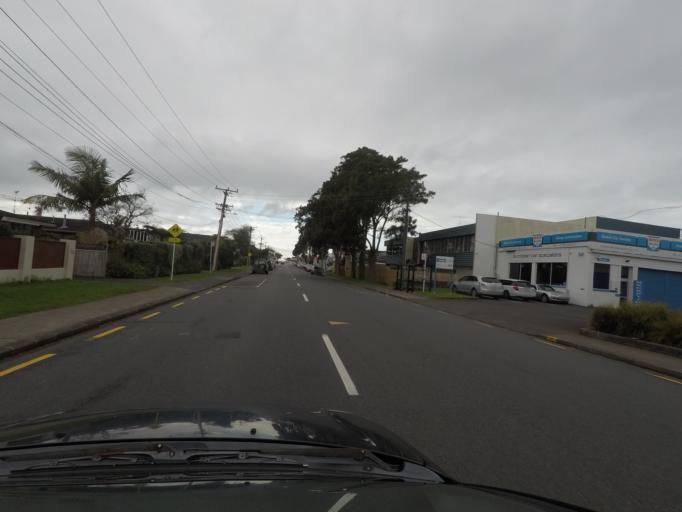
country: NZ
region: Auckland
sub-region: Auckland
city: Rothesay Bay
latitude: -36.7168
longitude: 174.7437
